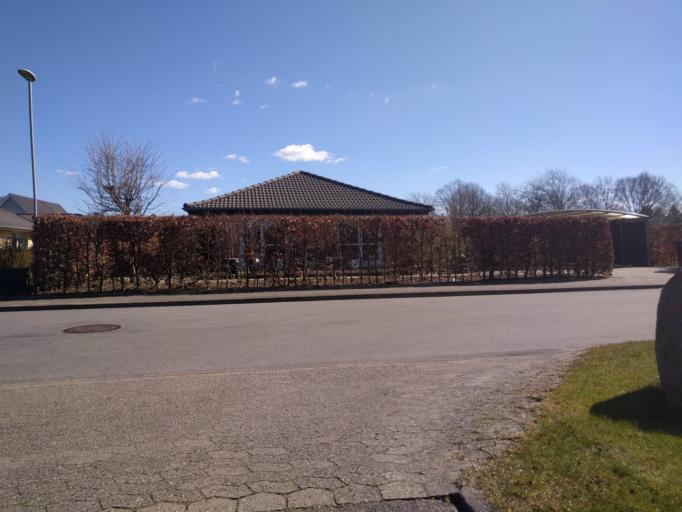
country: DK
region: South Denmark
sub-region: Kerteminde Kommune
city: Langeskov
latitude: 55.3646
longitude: 10.5900
